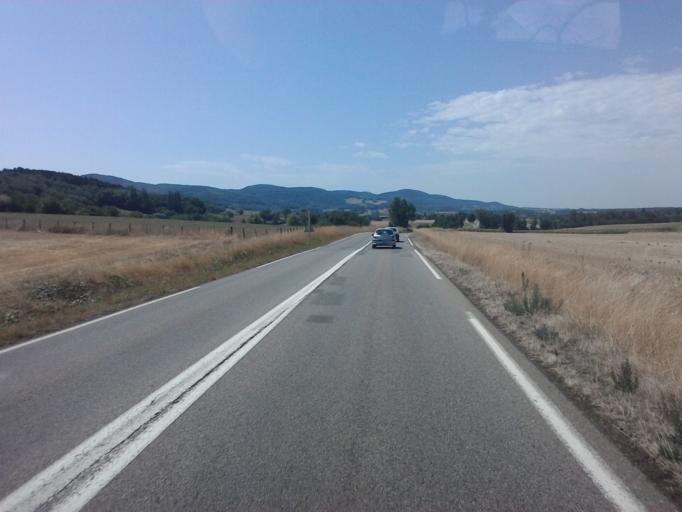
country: FR
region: Franche-Comte
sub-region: Departement du Jura
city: Montmorot
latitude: 46.6253
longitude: 5.4879
